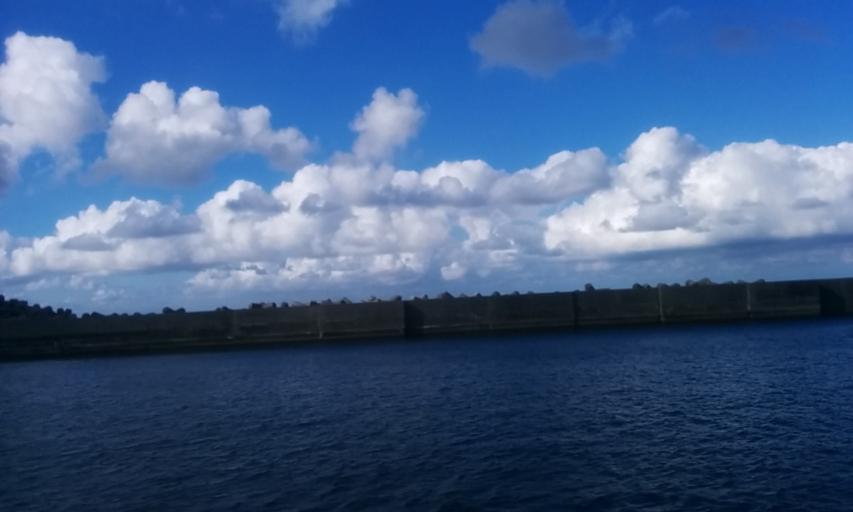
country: JP
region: Kagoshima
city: Nishinoomote
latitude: 30.4309
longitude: 130.5761
